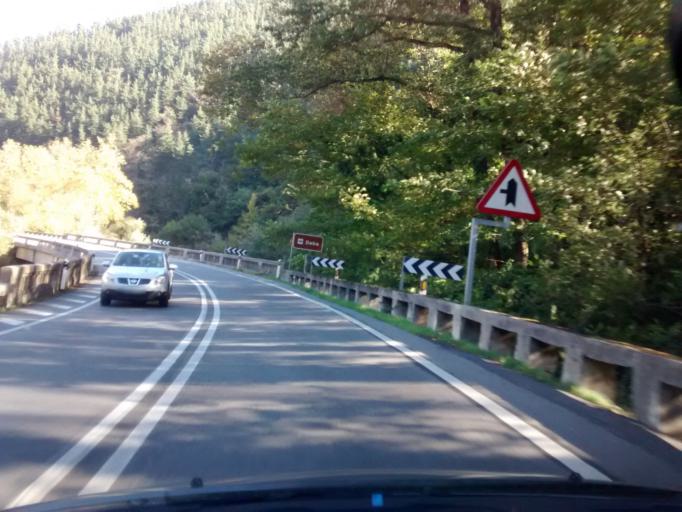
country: ES
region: Basque Country
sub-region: Provincia de Guipuzcoa
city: Mendaro
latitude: 43.2365
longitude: -2.3987
